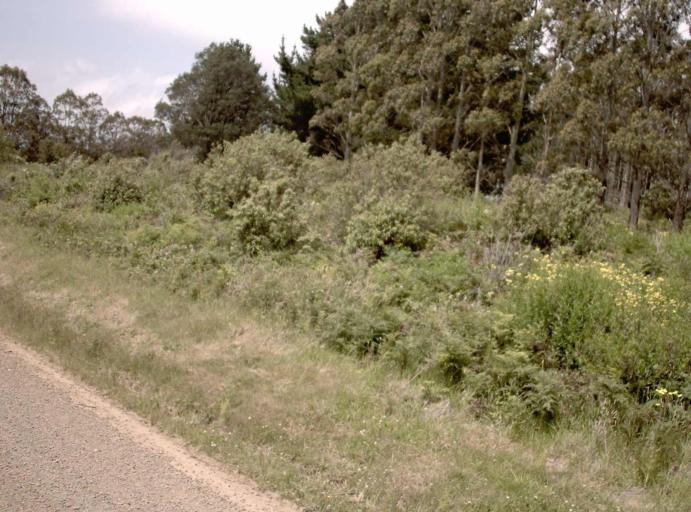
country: AU
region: Victoria
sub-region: Latrobe
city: Traralgon
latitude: -38.4171
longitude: 146.6124
